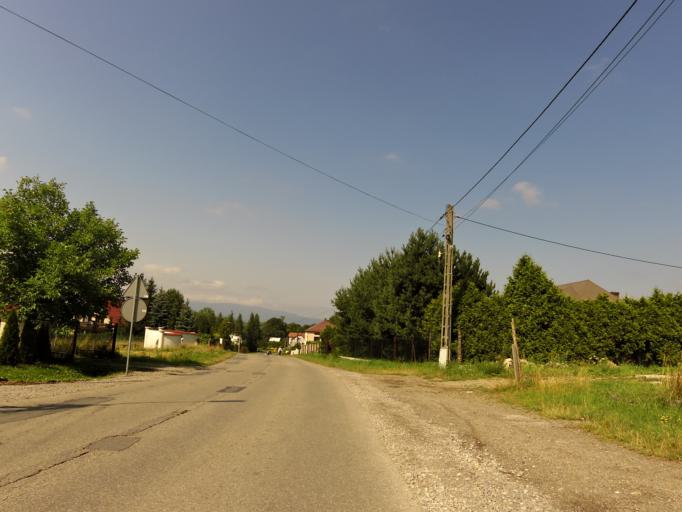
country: PL
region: Silesian Voivodeship
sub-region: Powiat zywiecki
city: Wieprz
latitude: 49.6271
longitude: 19.1695
